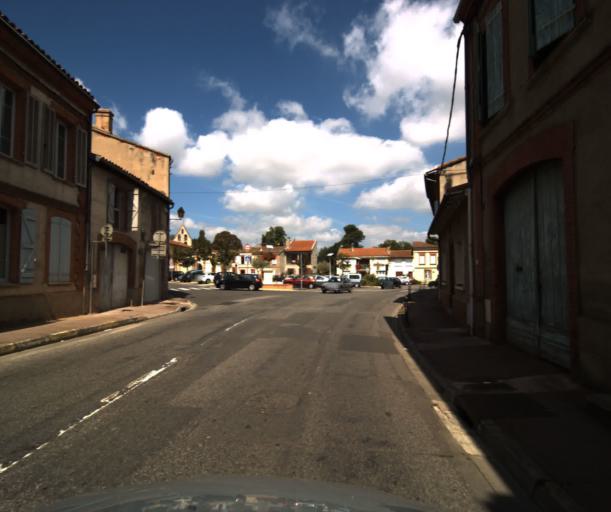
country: FR
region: Midi-Pyrenees
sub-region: Departement de la Haute-Garonne
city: Pinsaguel
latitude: 43.5096
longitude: 1.3890
